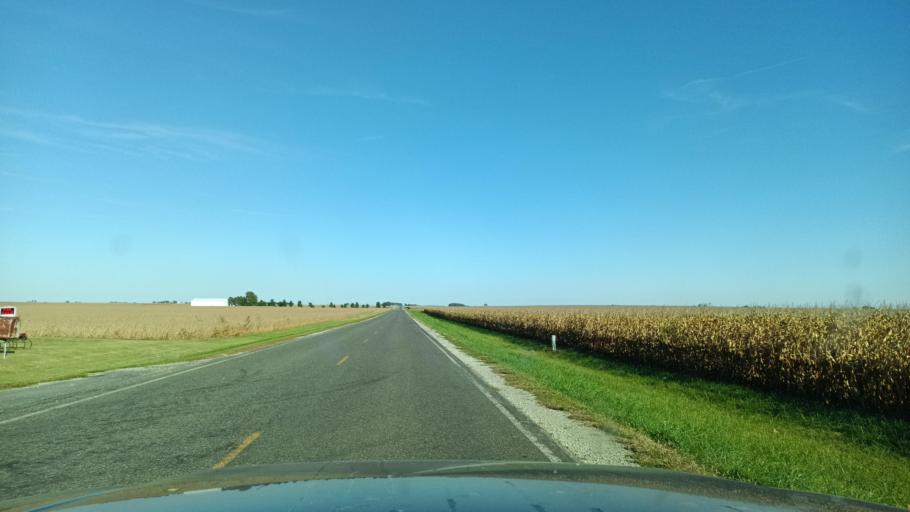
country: US
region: Illinois
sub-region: De Witt County
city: Clinton
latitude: 40.2243
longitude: -88.9546
